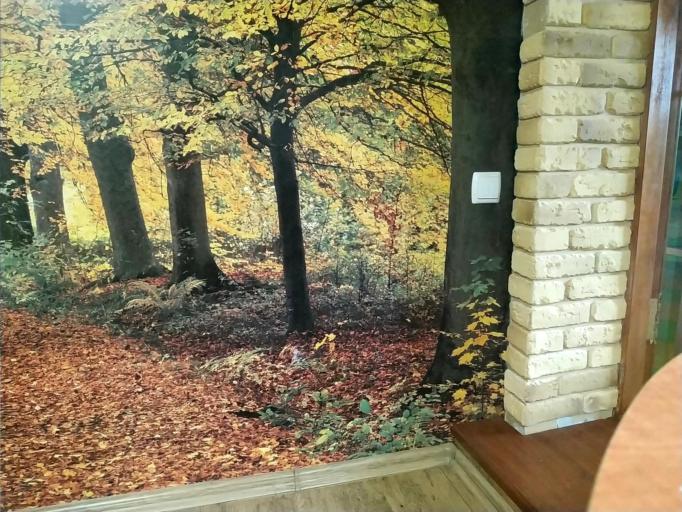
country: RU
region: Smolensk
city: Verkhnedneprovskiy
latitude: 54.9841
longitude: 33.2759
